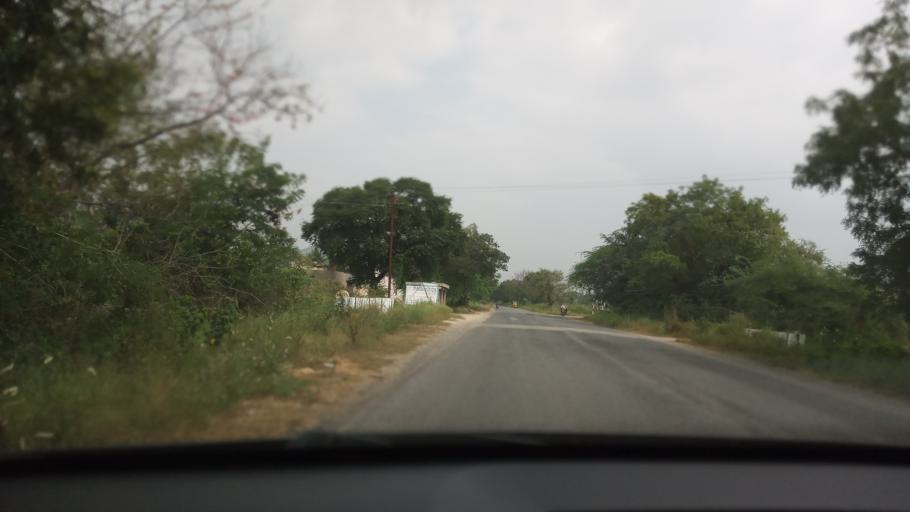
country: IN
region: Andhra Pradesh
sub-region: Chittoor
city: Madanapalle
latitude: 13.6519
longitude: 78.8302
